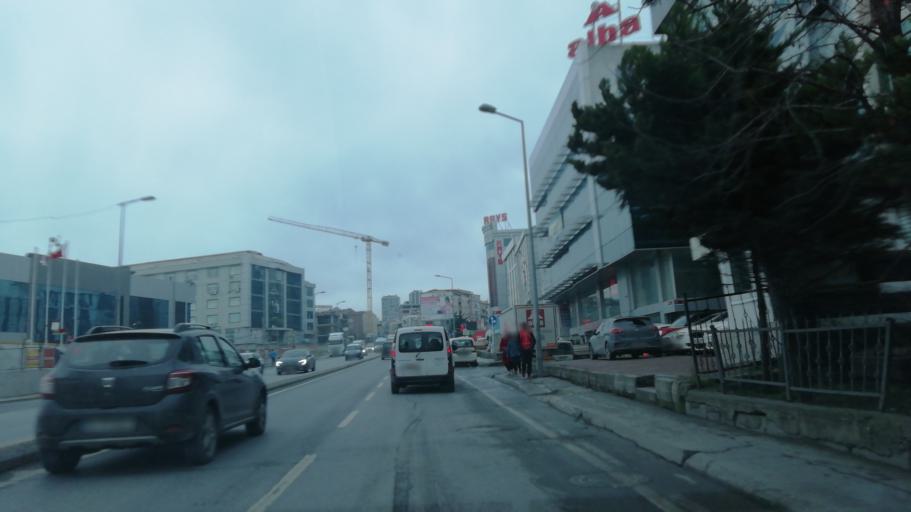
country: TR
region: Istanbul
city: Mahmutbey
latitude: 41.0452
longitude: 28.8148
